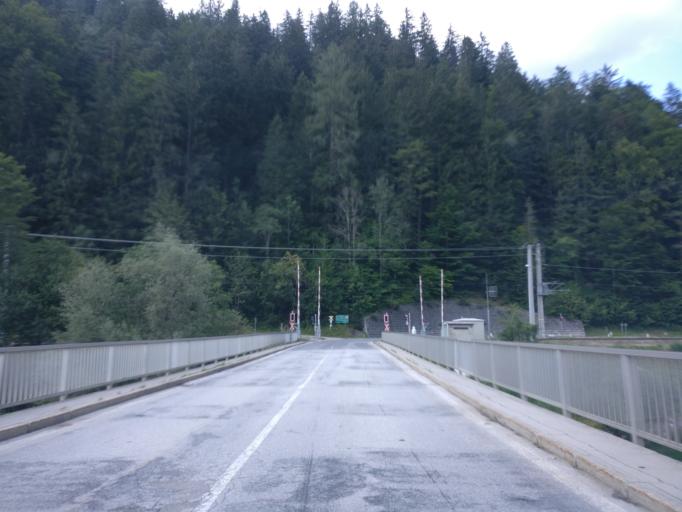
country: AT
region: Styria
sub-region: Politischer Bezirk Liezen
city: Johnsbach
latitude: 47.5907
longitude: 14.6286
